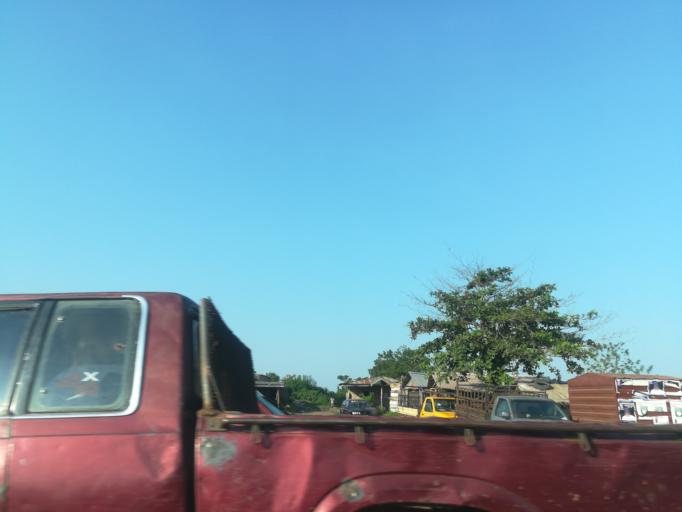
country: NG
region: Ogun
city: Abeokuta
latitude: 7.1825
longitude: 3.2791
